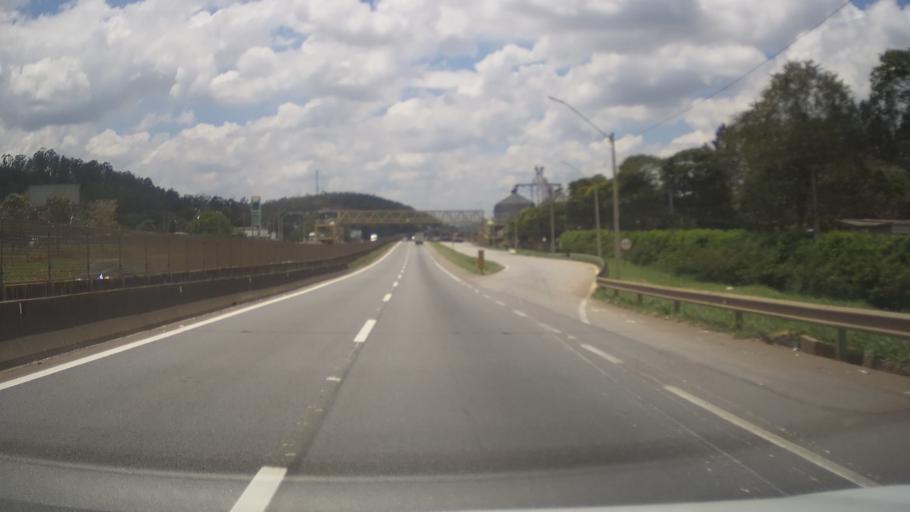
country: BR
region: Minas Gerais
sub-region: Tres Coracoes
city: Tres Coracoes
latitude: -21.6693
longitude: -45.3273
